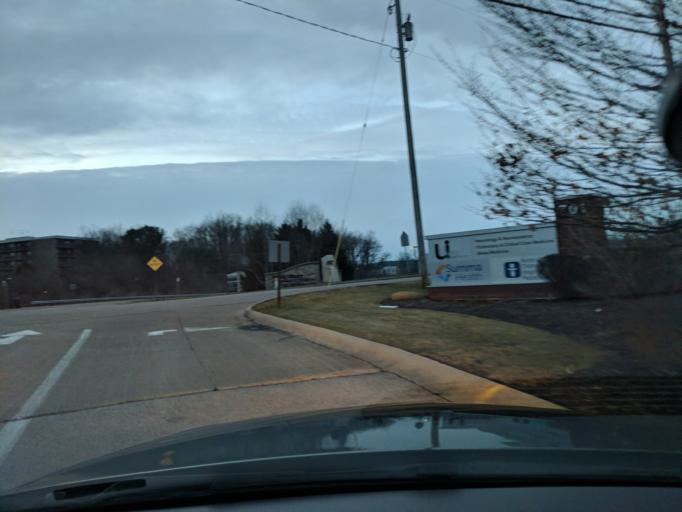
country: US
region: Ohio
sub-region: Summit County
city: Fairlawn
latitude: 41.0972
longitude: -81.5884
